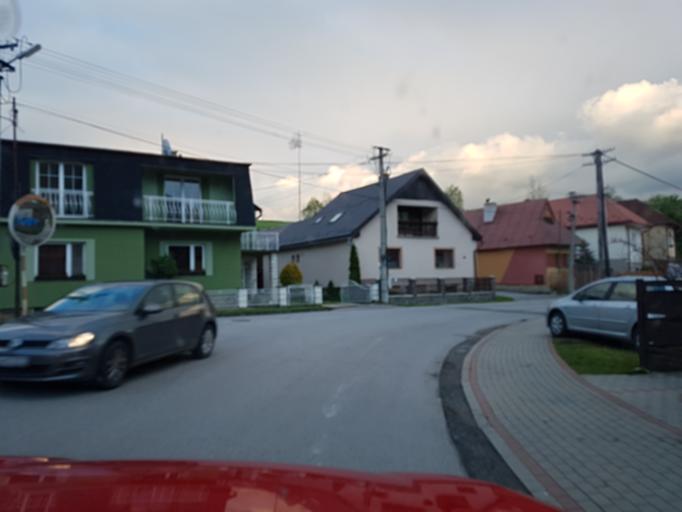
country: SK
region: Zilinsky
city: Ruzomberok
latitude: 49.1271
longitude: 19.4049
